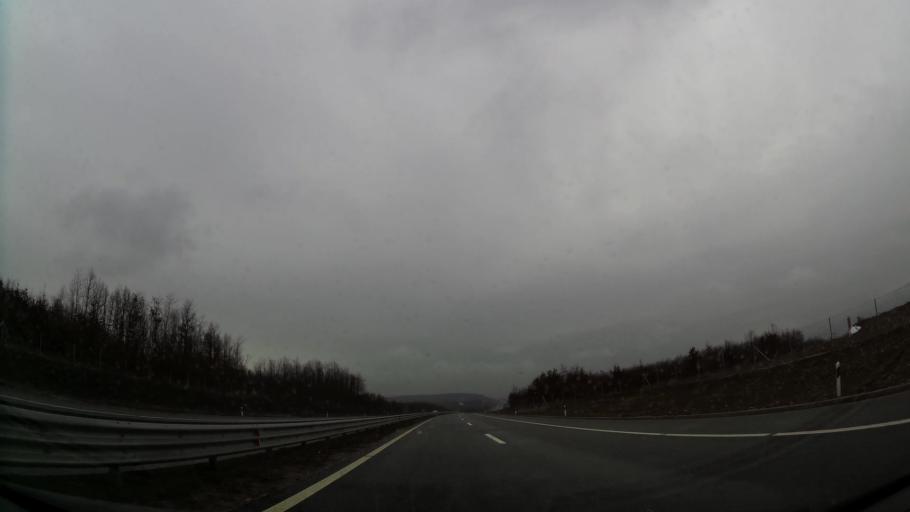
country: XK
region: Ferizaj
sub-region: Komuna e Ferizajt
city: Ferizaj
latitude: 42.3479
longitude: 21.2054
